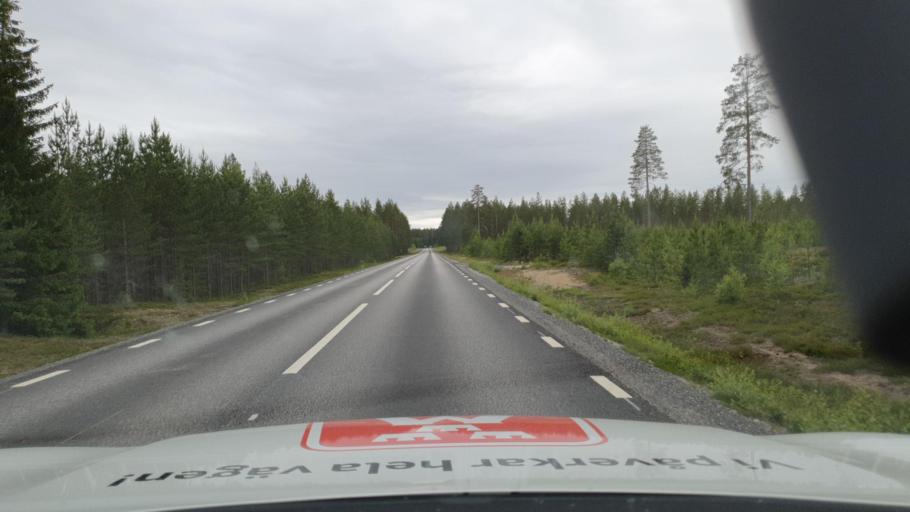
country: SE
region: Vaesterbotten
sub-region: Nordmalings Kommun
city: Nordmaling
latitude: 63.7073
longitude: 19.6302
